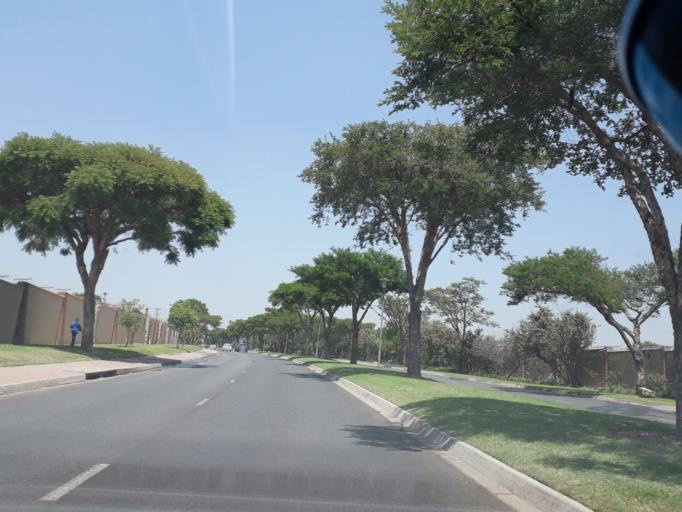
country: ZA
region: Gauteng
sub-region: City of Johannesburg Metropolitan Municipality
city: Midrand
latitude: -26.0267
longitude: 28.0820
